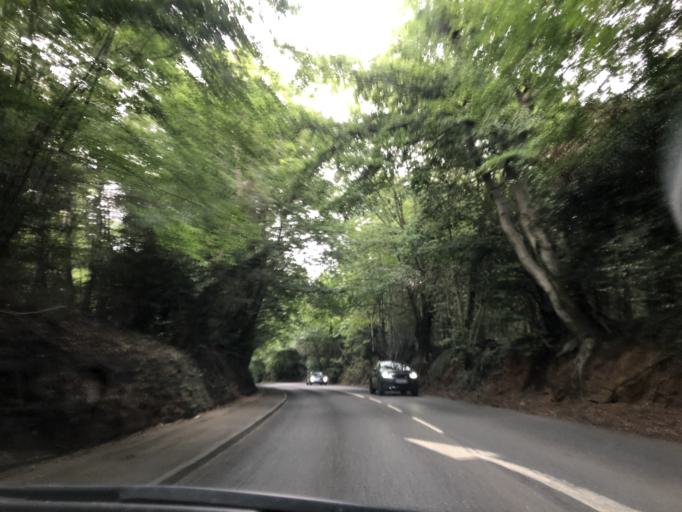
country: GB
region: England
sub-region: Kent
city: Sevenoaks
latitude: 51.2562
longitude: 0.1993
